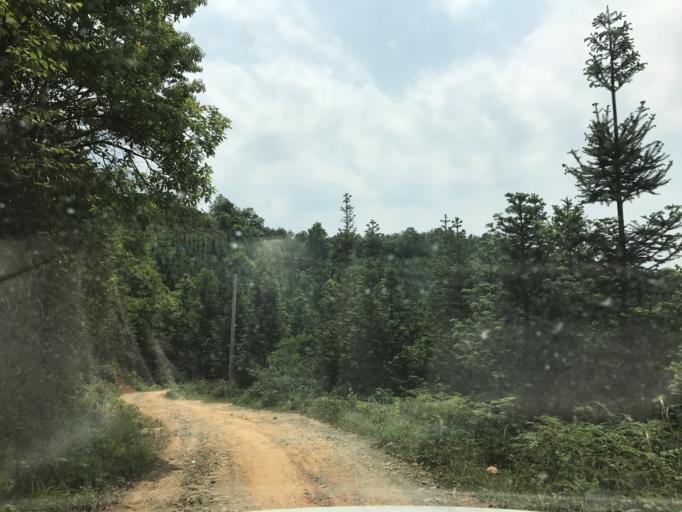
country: CN
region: Guangxi Zhuangzu Zizhiqu
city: Xinzhou
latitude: 24.9864
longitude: 105.9378
